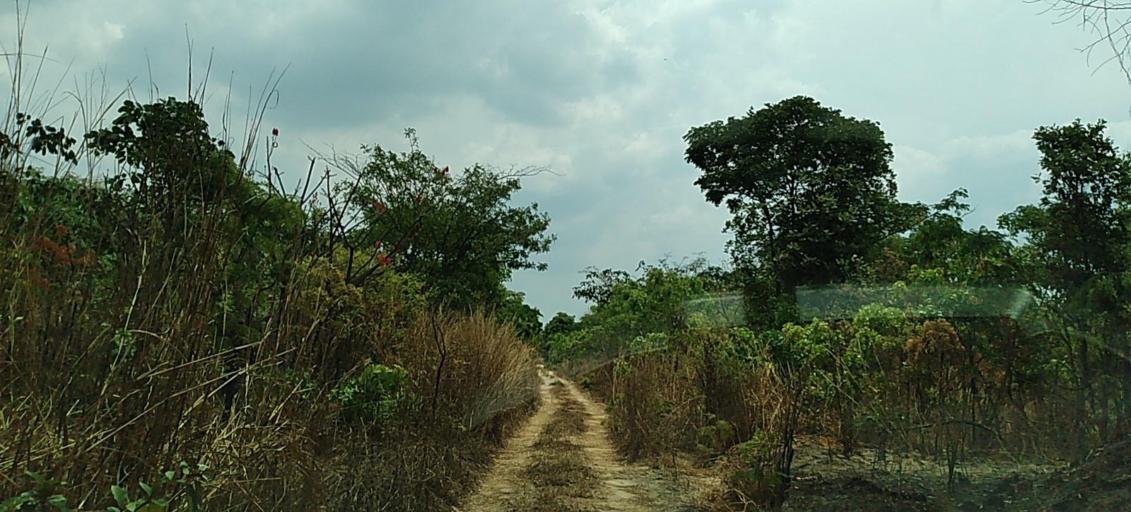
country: ZM
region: Copperbelt
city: Chililabombwe
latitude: -12.3294
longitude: 27.7698
